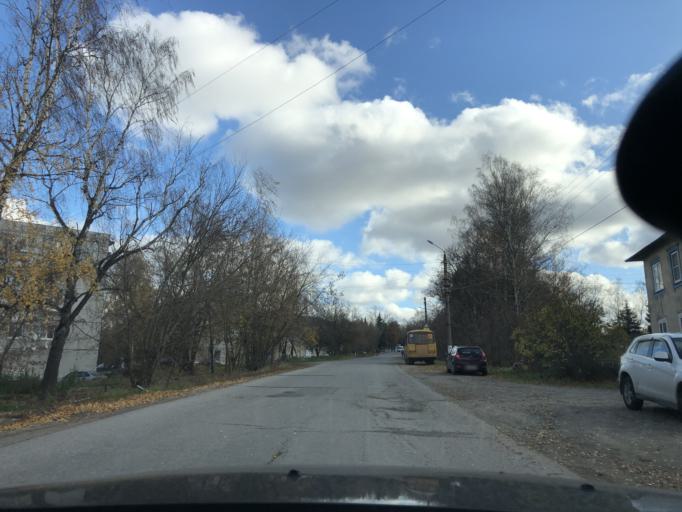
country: RU
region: Tula
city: Gorelki
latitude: 54.2960
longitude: 37.5662
